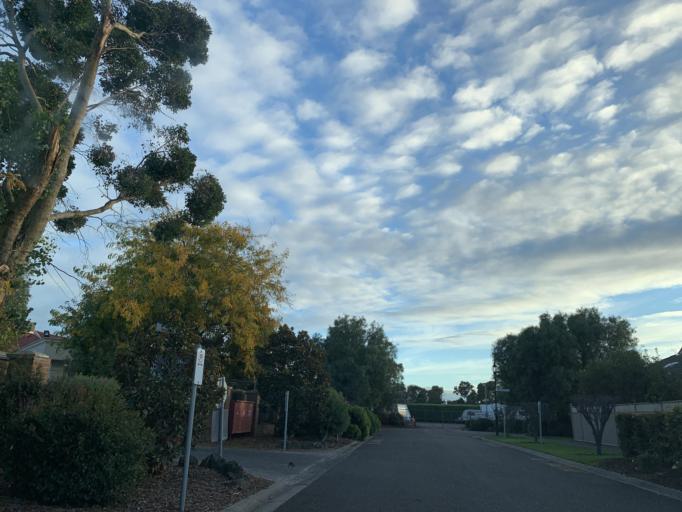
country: AU
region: Victoria
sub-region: Casey
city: Cranbourne East
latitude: -38.1129
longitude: 145.3005
